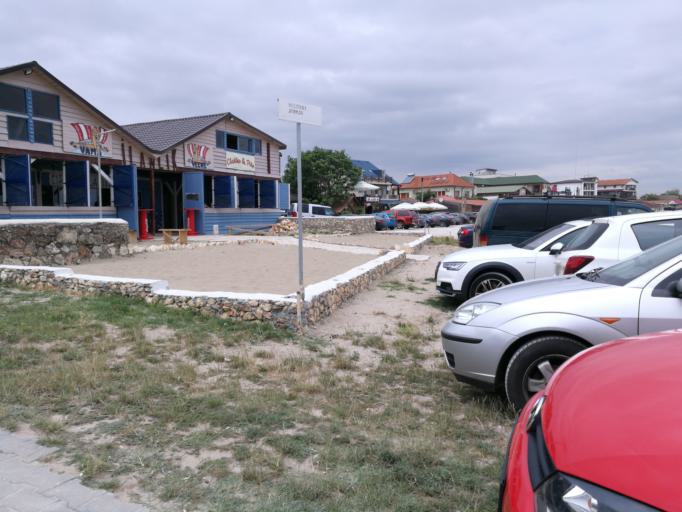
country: RO
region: Constanta
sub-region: Municipiul Mangalia
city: Mangalia
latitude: 43.7522
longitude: 28.5751
